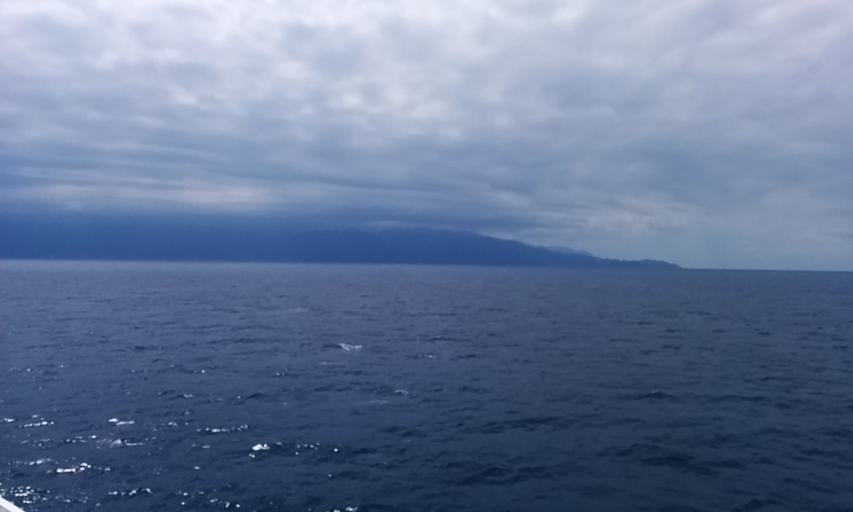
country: JP
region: Kagoshima
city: Nishinoomote
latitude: 30.5436
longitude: 130.6166
